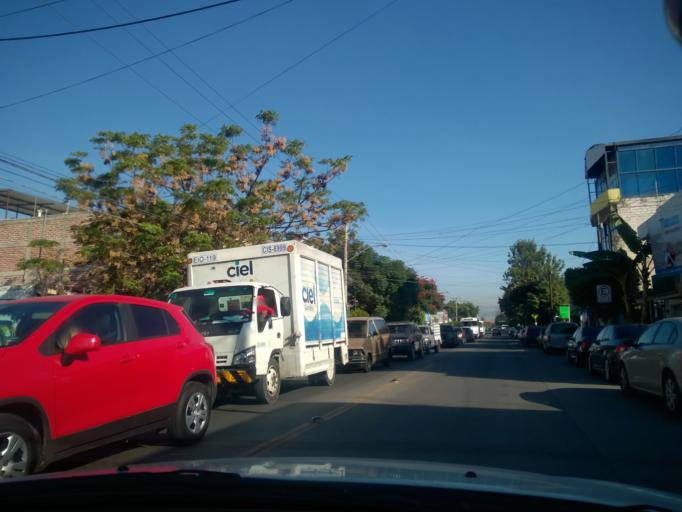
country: MX
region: Guanajuato
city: Leon
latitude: 21.1015
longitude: -101.6493
